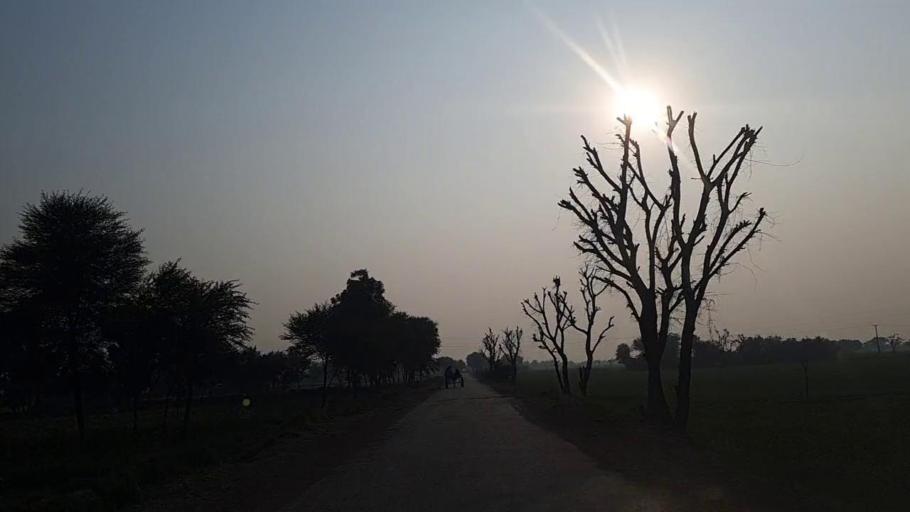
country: PK
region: Sindh
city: Nawabshah
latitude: 26.2279
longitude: 68.4825
